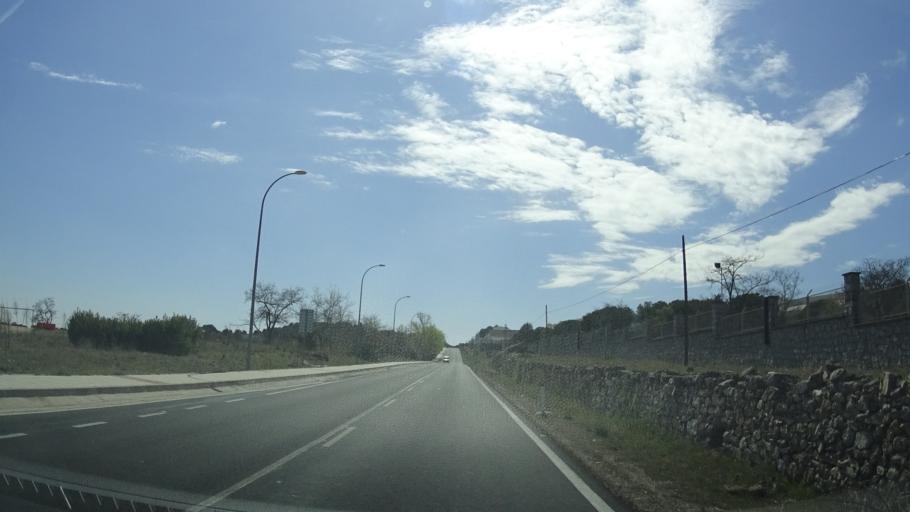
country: ES
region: Madrid
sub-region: Provincia de Madrid
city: Hoyo de Manzanares
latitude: 40.6285
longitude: -3.8774
